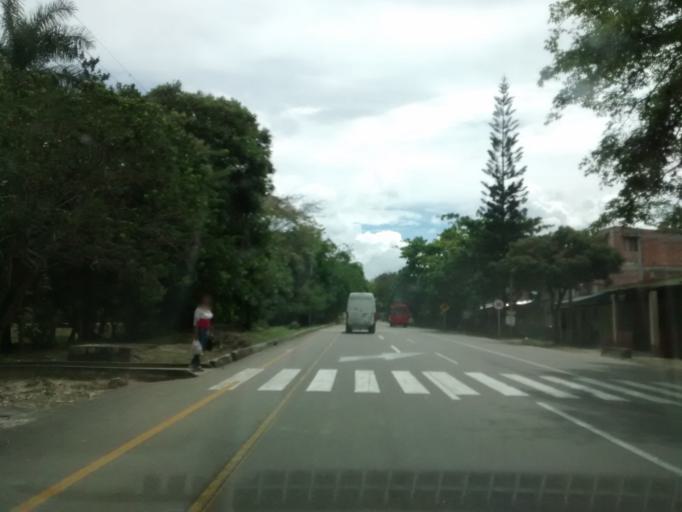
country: CO
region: Tolima
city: Ibague
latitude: 4.4026
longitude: -75.1521
